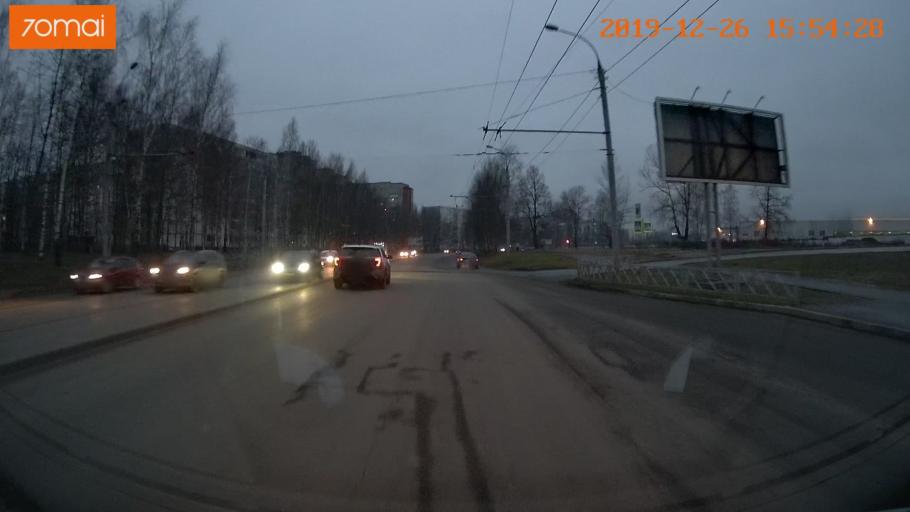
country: RU
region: Jaroslavl
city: Rybinsk
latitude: 58.0449
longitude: 38.8186
